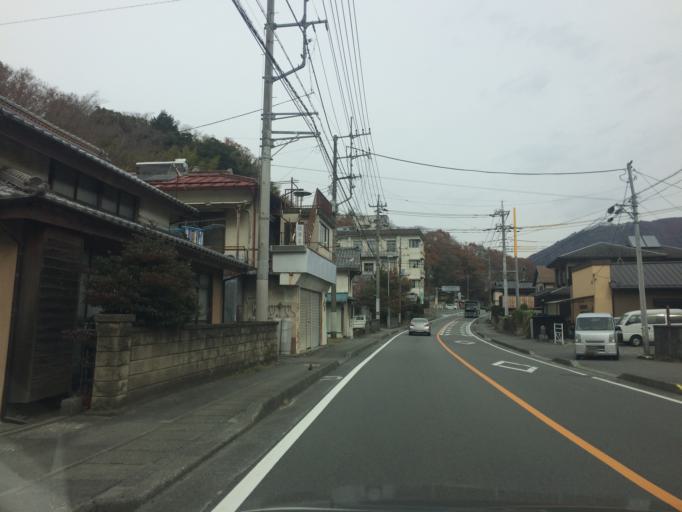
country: JP
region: Yamanashi
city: Ryuo
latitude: 35.4148
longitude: 138.4427
